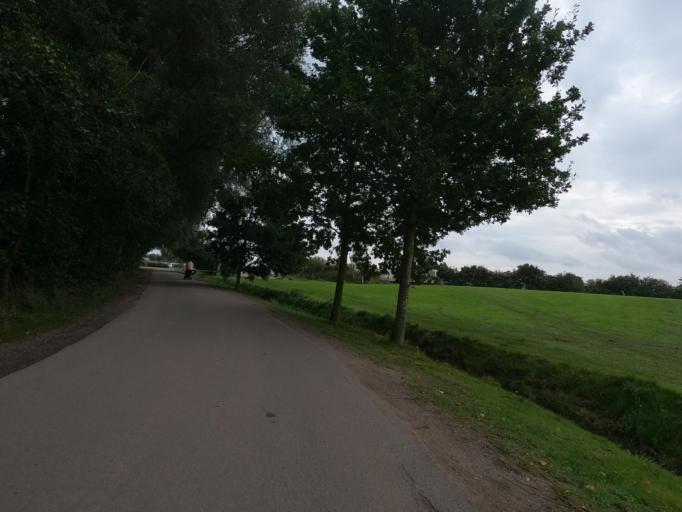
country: DE
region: Schleswig-Holstein
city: Grossenbrode
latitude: 54.3442
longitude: 11.0607
